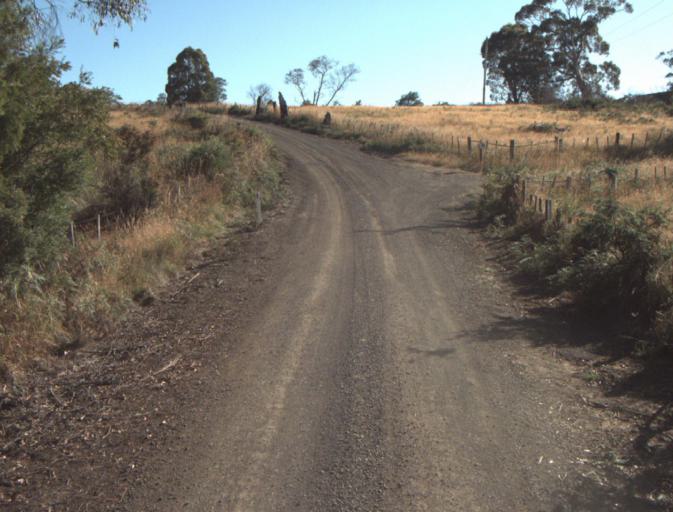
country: AU
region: Tasmania
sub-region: Launceston
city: Newstead
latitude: -41.4113
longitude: 147.2882
